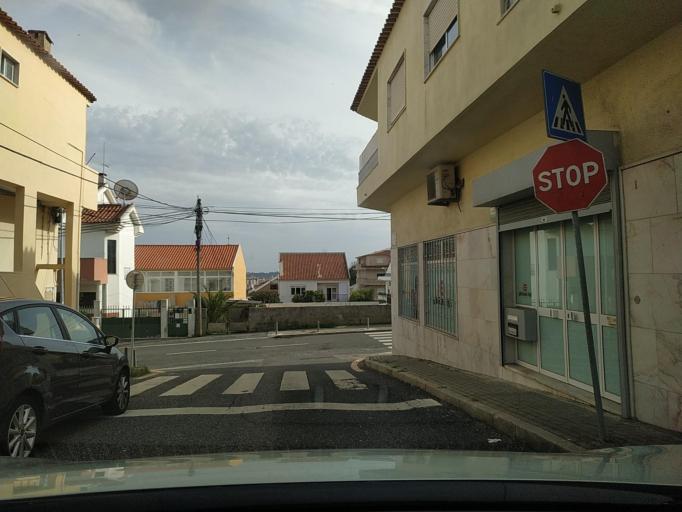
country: PT
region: Lisbon
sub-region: Amadora
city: Amadora
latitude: 38.7745
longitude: -9.2369
